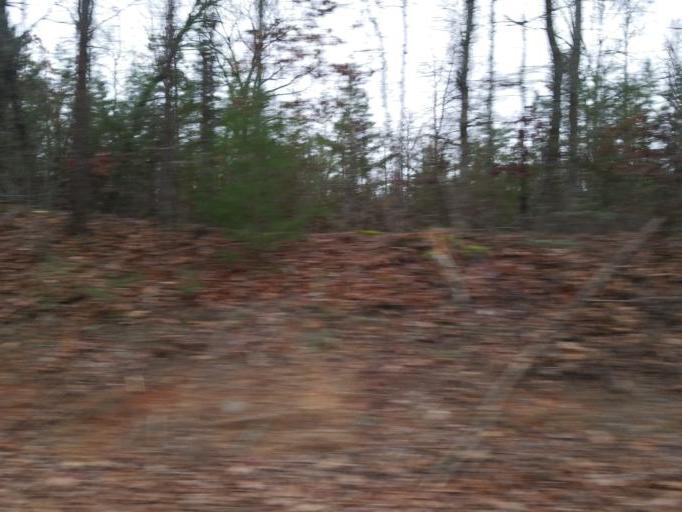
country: US
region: Georgia
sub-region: Dawson County
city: Dawsonville
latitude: 34.5111
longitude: -84.2234
